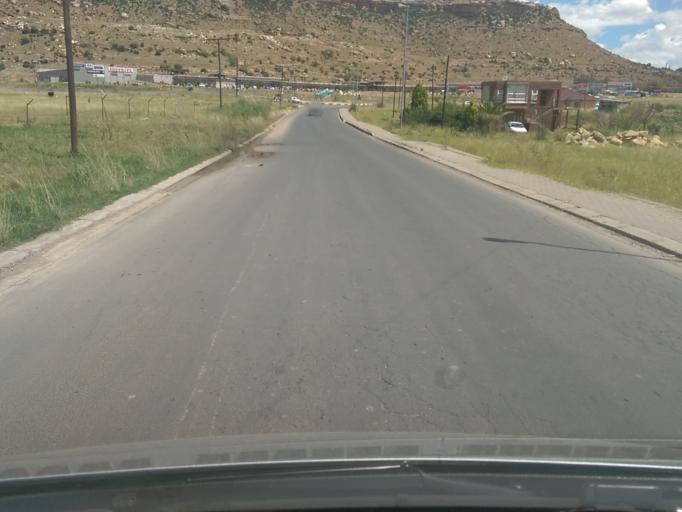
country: LS
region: Maseru
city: Maseru
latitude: -29.3311
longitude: 27.4859
